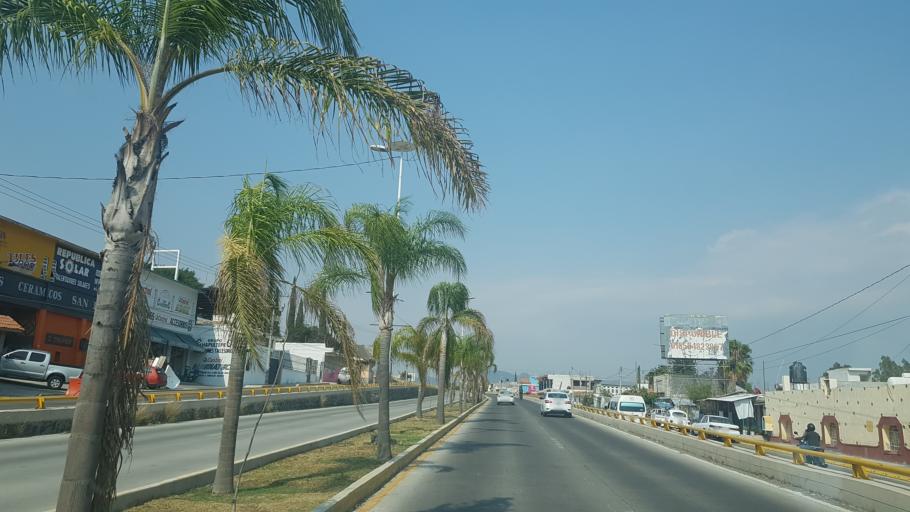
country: MX
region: Puebla
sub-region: Atlixco
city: El Encanto del Cerril
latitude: 18.9199
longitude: -98.4186
